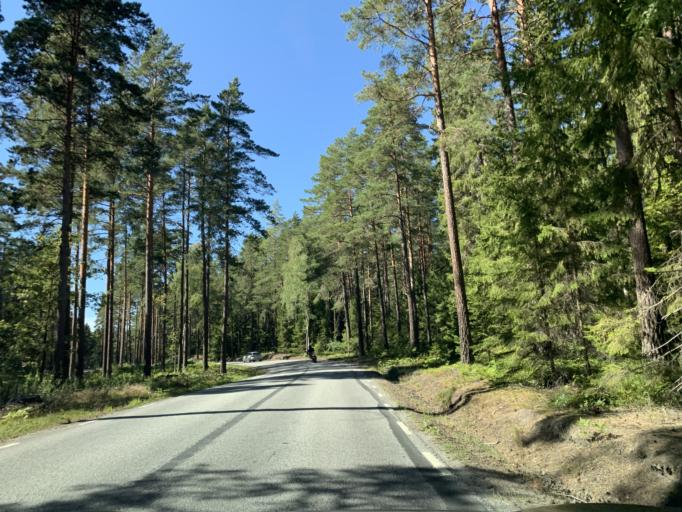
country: SE
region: Stockholm
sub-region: Ekero Kommun
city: Ekeroe
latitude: 59.2723
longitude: 17.8326
